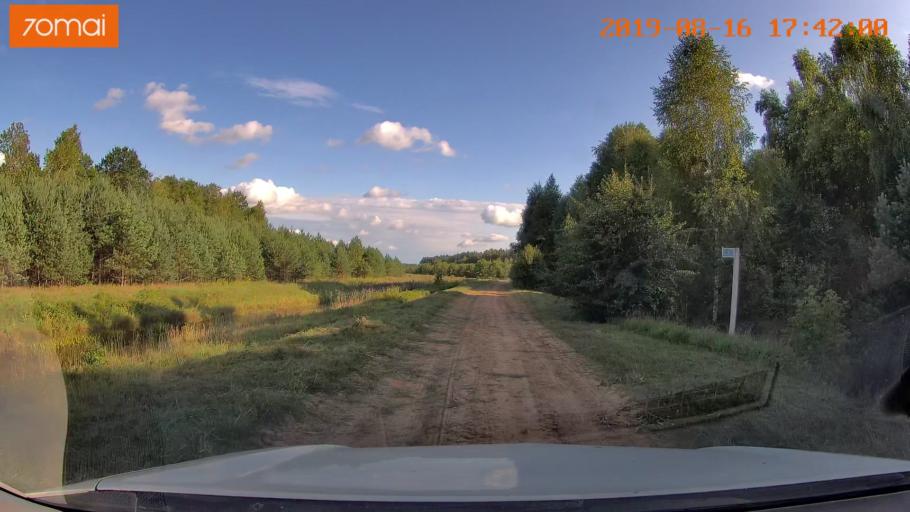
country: BY
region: Mogilev
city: Asipovichy
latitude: 53.2382
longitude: 28.6650
